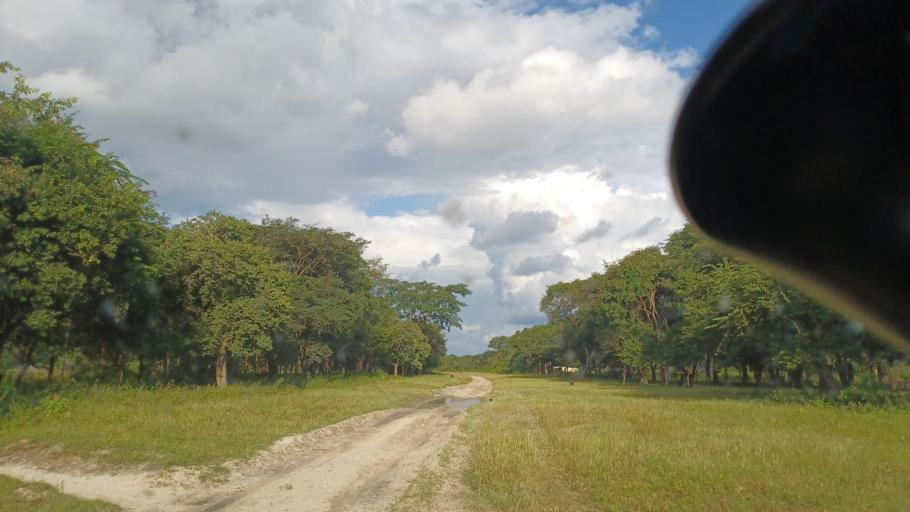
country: ZM
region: North-Western
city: Kabompo
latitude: -13.2453
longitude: 24.0204
